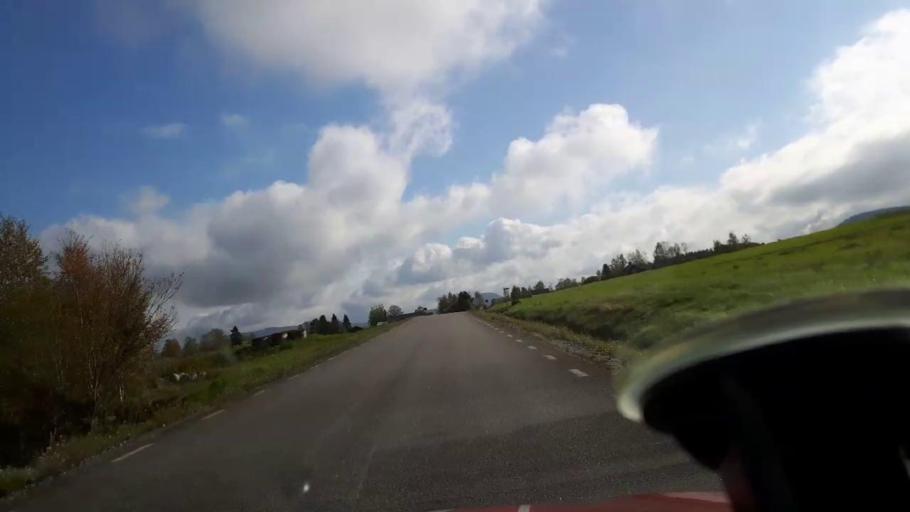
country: SE
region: Gaevleborg
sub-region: Ljusdals Kommun
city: Jaervsoe
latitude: 61.7565
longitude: 16.1157
